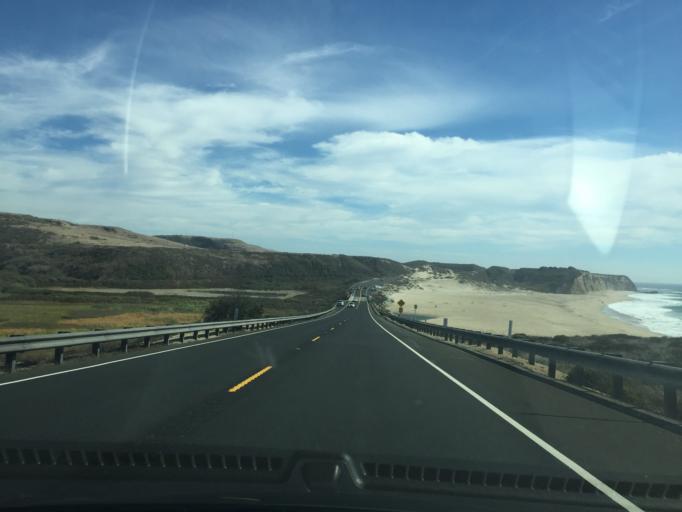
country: US
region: California
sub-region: Santa Cruz County
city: Bonny Doon
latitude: 37.0427
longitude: -122.2314
